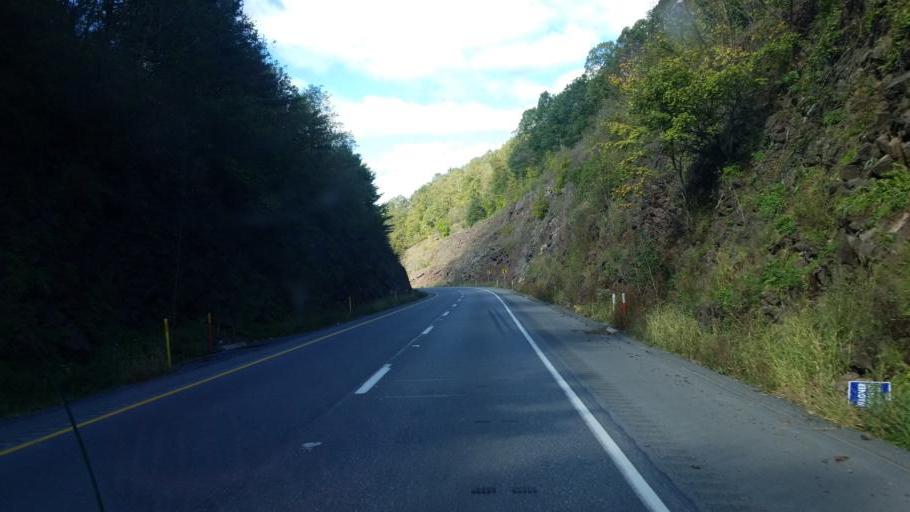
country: US
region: Pennsylvania
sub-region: Bedford County
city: Earlston
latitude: 39.9971
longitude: -78.2621
